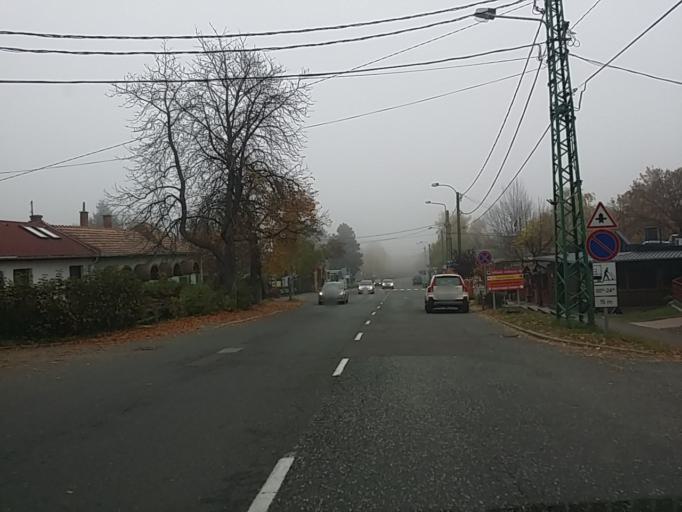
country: HU
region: Heves
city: Gyongyossolymos
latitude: 47.8319
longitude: 19.9693
